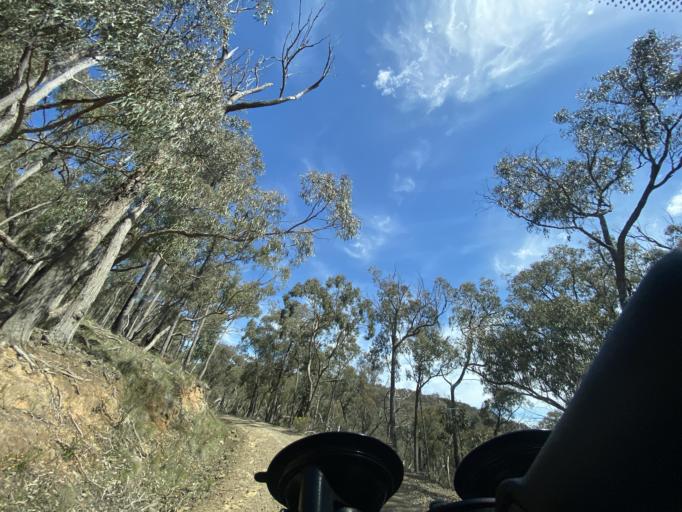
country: AU
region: Victoria
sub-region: Mansfield
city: Mansfield
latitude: -36.8043
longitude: 146.1076
